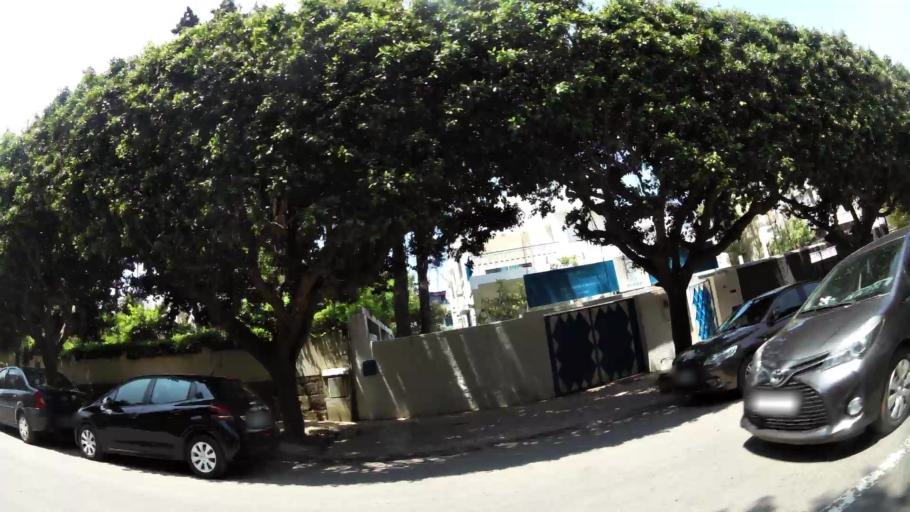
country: MA
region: Rabat-Sale-Zemmour-Zaer
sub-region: Rabat
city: Rabat
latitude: 34.0120
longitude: -6.8260
